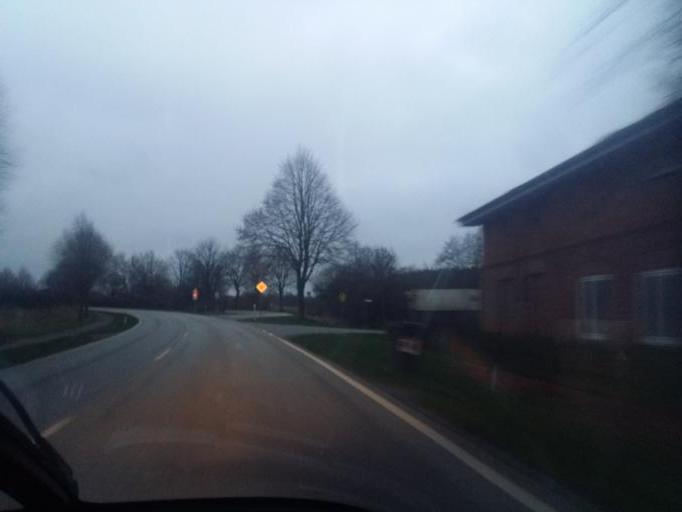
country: DE
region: Schleswig-Holstein
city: Gokels
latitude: 54.1180
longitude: 9.4487
